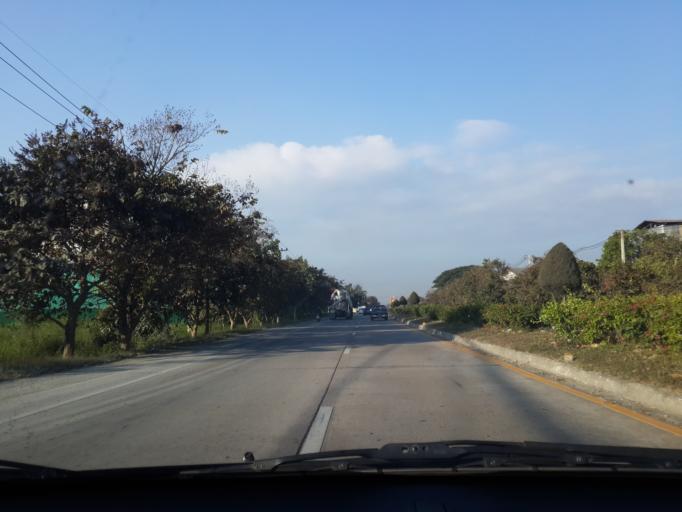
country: TH
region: Chiang Mai
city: San Sai
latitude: 18.8584
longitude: 99.1048
